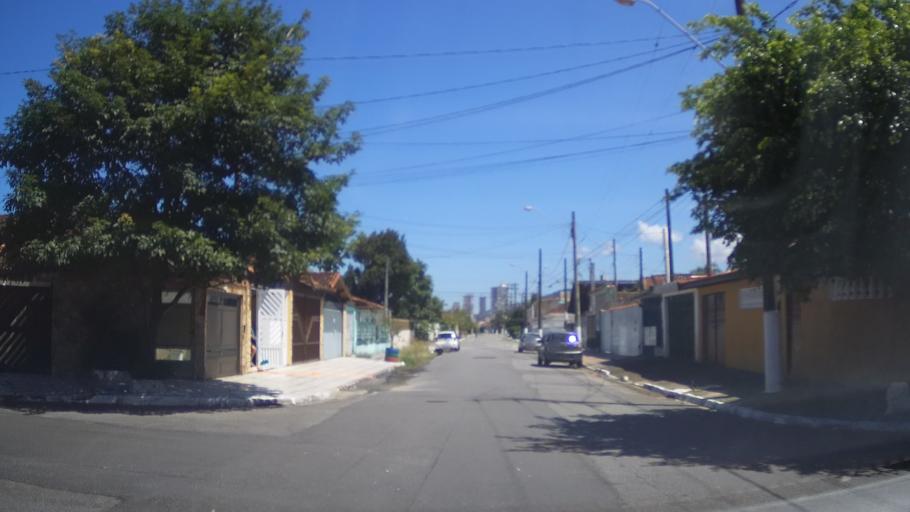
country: BR
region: Sao Paulo
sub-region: Mongagua
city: Mongagua
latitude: -24.0426
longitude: -46.5171
